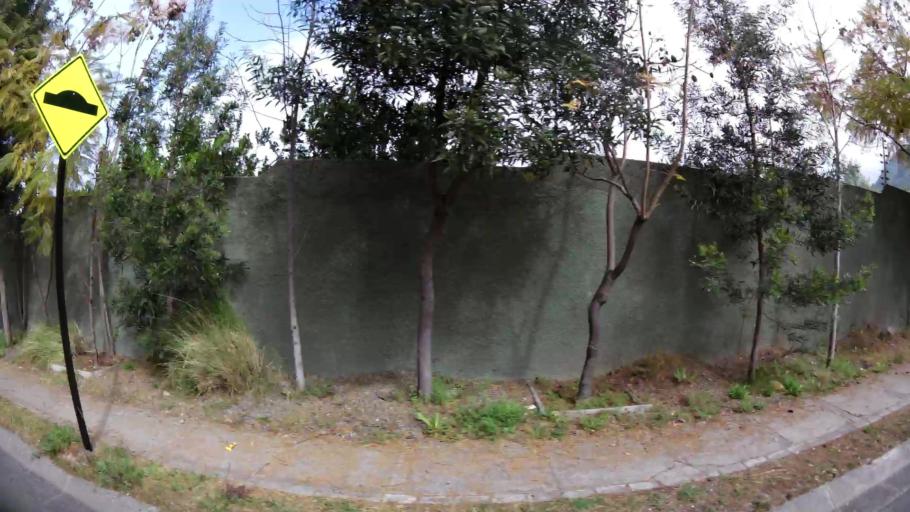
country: CL
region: Santiago Metropolitan
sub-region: Provincia de Santiago
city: Villa Presidente Frei, Nunoa, Santiago, Chile
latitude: -33.3681
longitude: -70.5714
